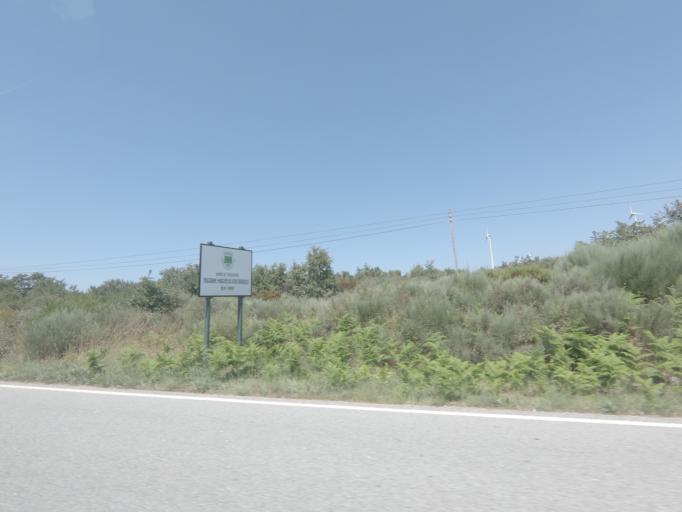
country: PT
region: Viseu
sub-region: Tarouca
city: Tarouca
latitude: 40.9963
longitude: -7.8842
